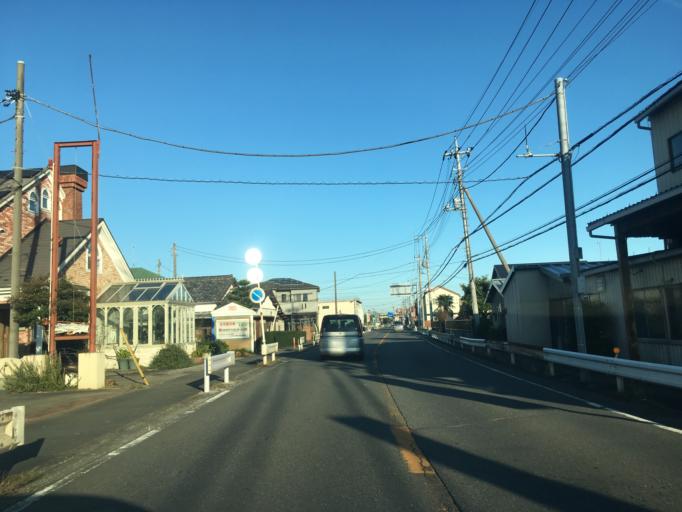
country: JP
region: Saitama
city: Kawagoe
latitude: 35.9654
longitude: 139.4688
